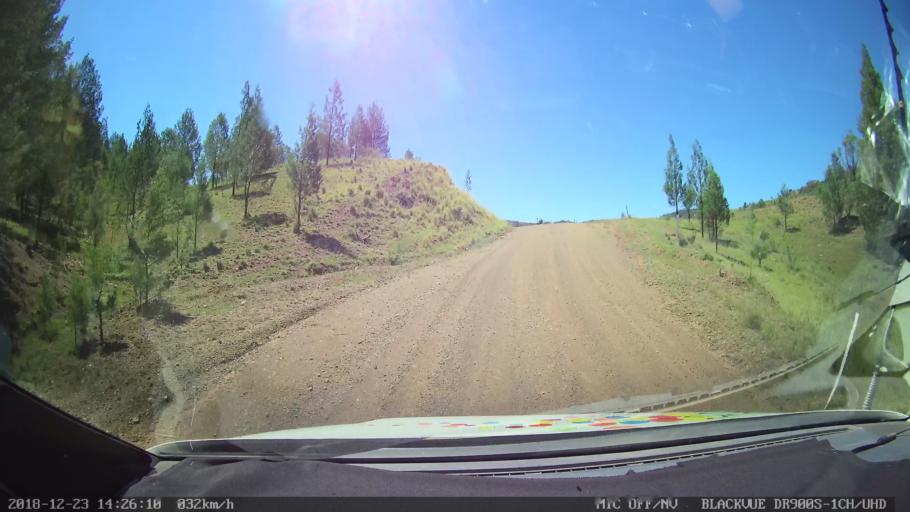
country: AU
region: New South Wales
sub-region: Tamworth Municipality
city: Manilla
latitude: -30.6241
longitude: 150.9534
